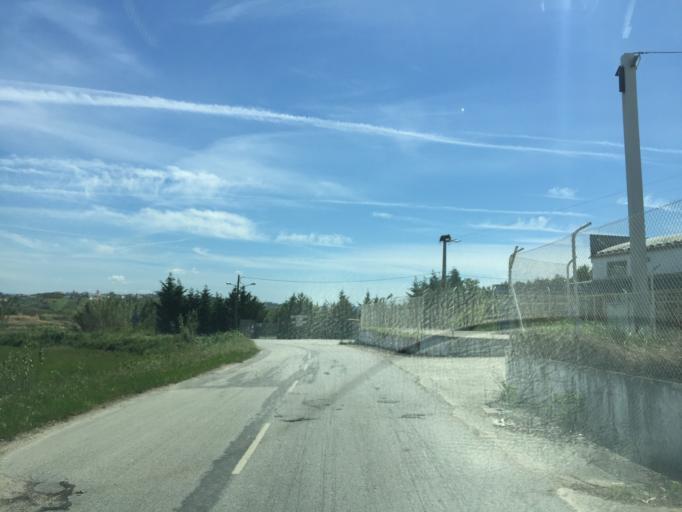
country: PT
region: Leiria
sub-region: Pombal
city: Lourical
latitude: 40.0683
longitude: -8.7463
